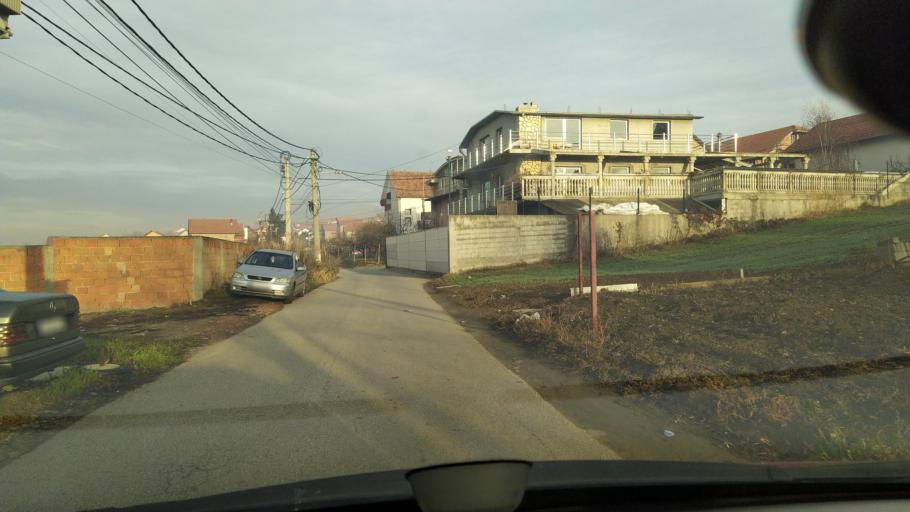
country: RS
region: Central Serbia
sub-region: Belgrade
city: Zvezdara
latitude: 44.7493
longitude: 20.5741
